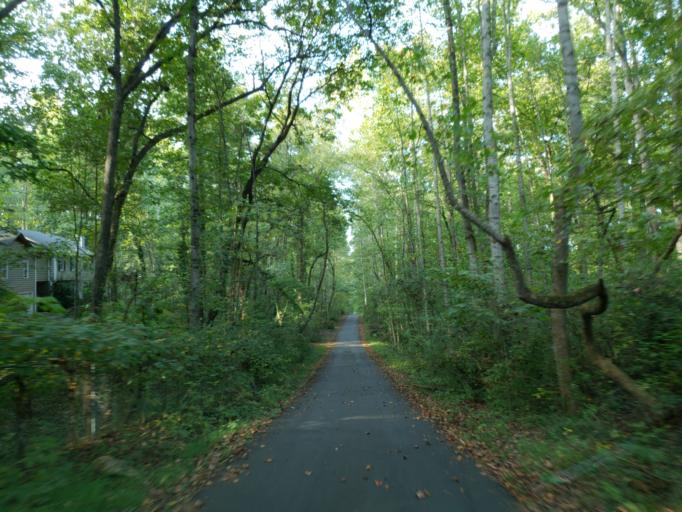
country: US
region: Georgia
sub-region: Fulton County
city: Roswell
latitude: 34.0809
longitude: -84.4069
